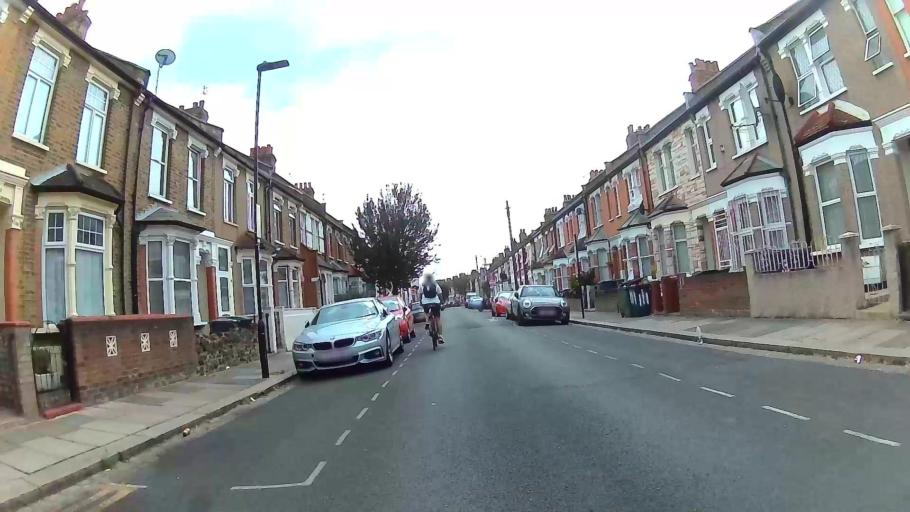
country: GB
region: England
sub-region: Greater London
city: Harringay
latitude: 51.5927
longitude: -0.0763
